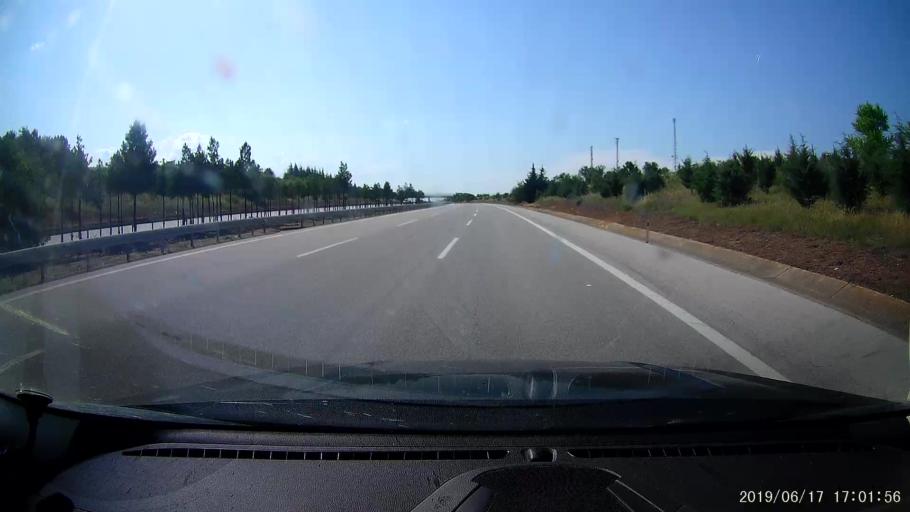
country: TR
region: Edirne
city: Haskoy
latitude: 41.6341
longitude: 26.7928
